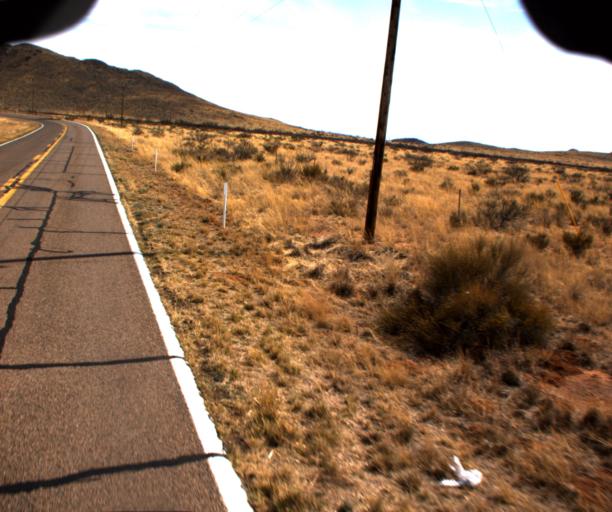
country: US
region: Arizona
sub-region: Cochise County
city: Willcox
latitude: 31.8788
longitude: -109.6612
